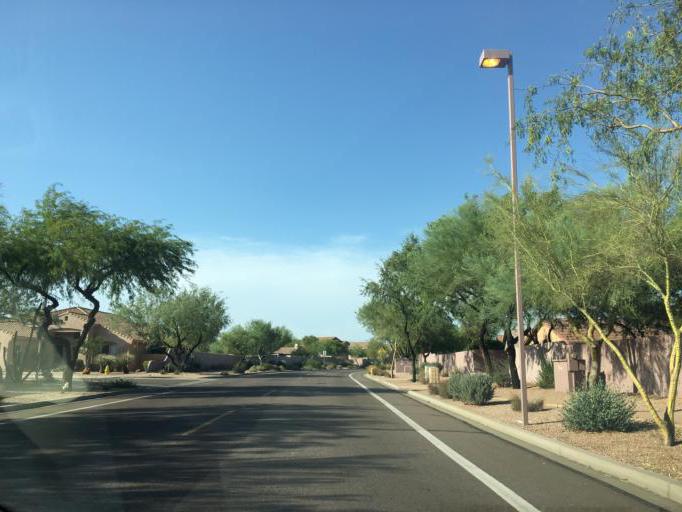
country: US
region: Arizona
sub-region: Maricopa County
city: Carefree
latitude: 33.6845
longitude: -111.9820
